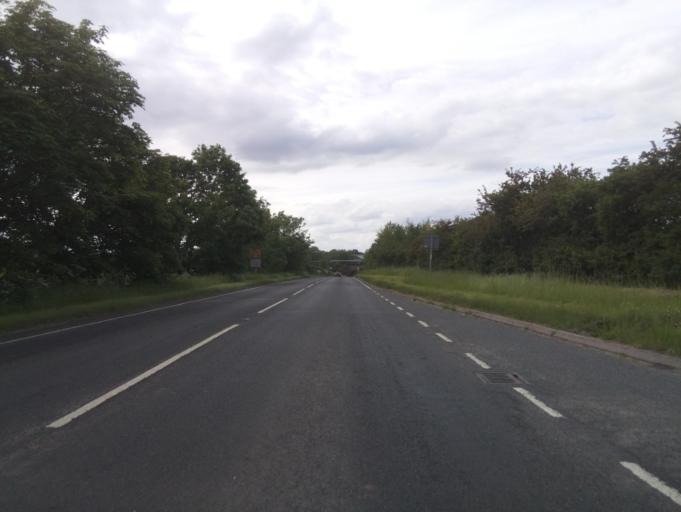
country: GB
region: England
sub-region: Worcestershire
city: Kempsey
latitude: 52.1542
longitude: -2.1518
